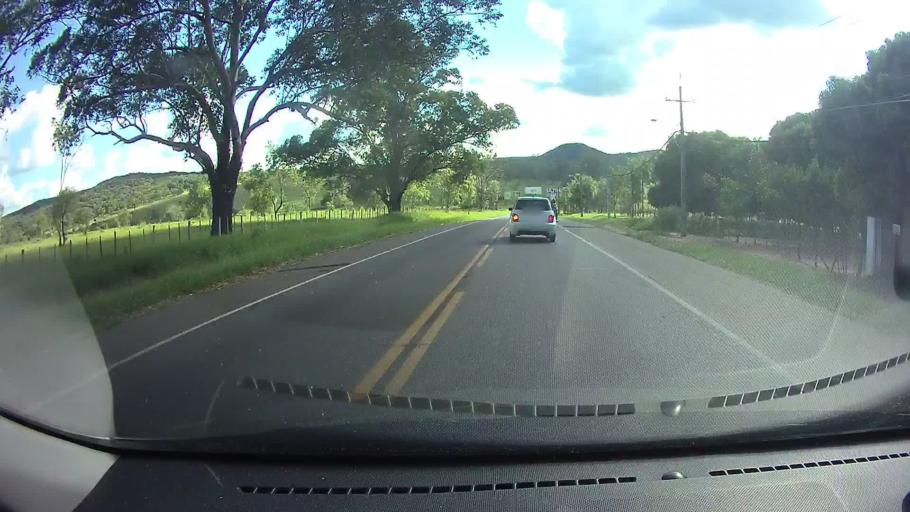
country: PY
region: Cordillera
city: Caacupe
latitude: -25.3864
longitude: -57.0584
